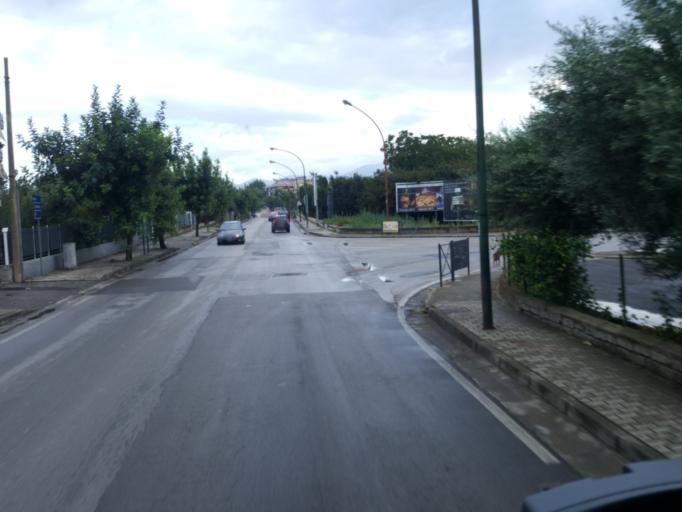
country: IT
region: Campania
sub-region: Provincia di Napoli
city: Palma Campania
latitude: 40.8641
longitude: 14.5485
